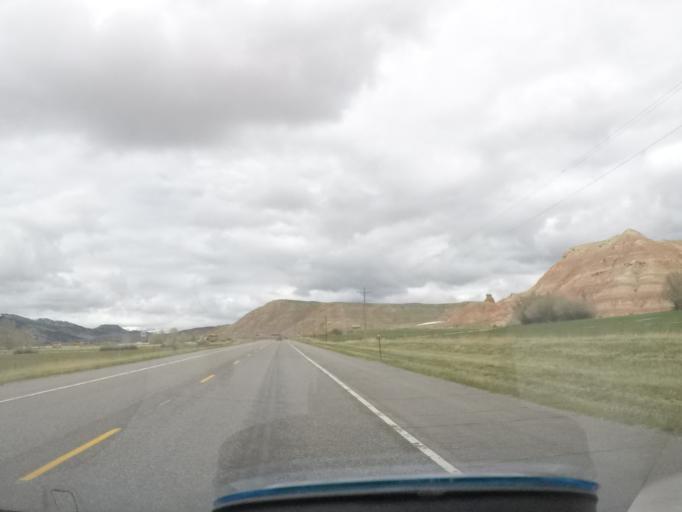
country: US
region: Wyoming
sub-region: Sublette County
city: Pinedale
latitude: 43.5628
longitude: -109.6999
